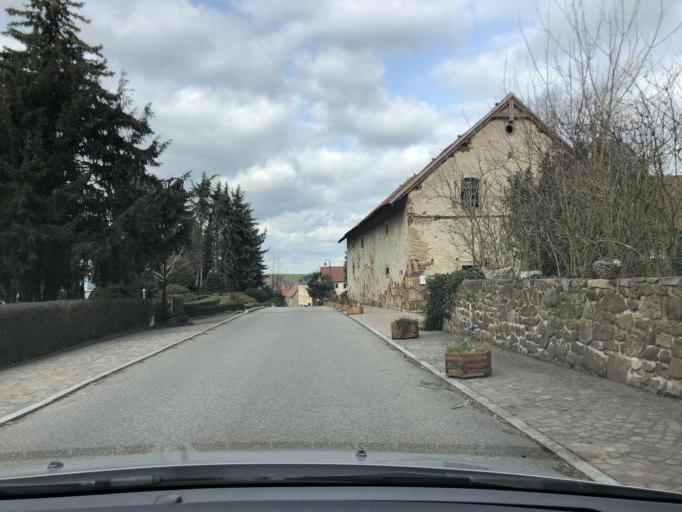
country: DE
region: Saxony
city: Bockelwitz
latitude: 51.1958
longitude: 12.9583
